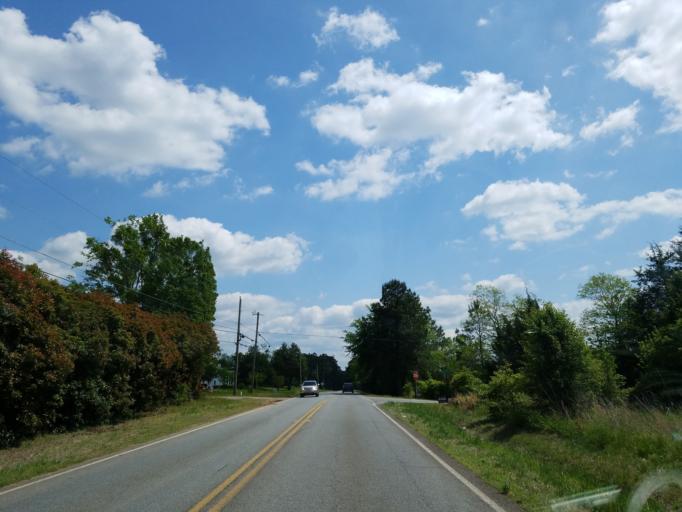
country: US
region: Georgia
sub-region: Monroe County
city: Forsyth
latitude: 33.0710
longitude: -83.9557
